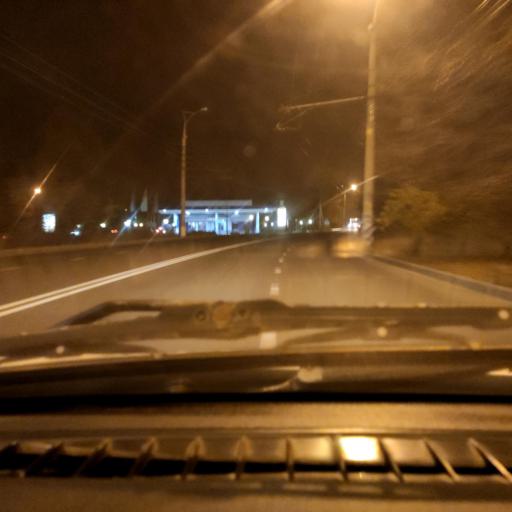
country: RU
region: Samara
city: Zhigulevsk
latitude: 53.5086
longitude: 49.4634
